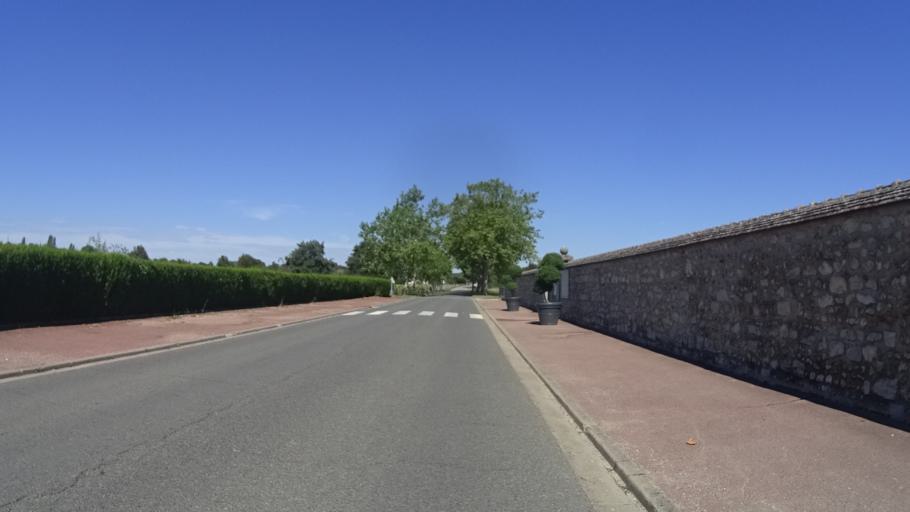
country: FR
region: Centre
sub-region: Departement du Cher
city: Belleville-sur-Loire
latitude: 47.5121
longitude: 2.8472
